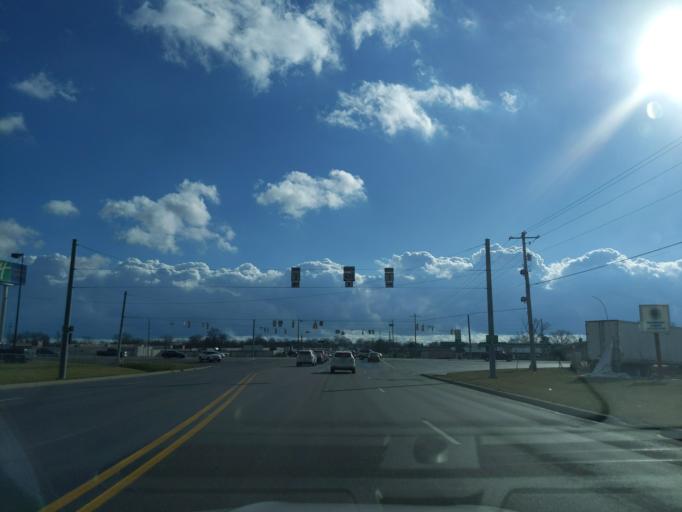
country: US
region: Indiana
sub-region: Decatur County
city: Greensburg
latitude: 39.3488
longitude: -85.4988
